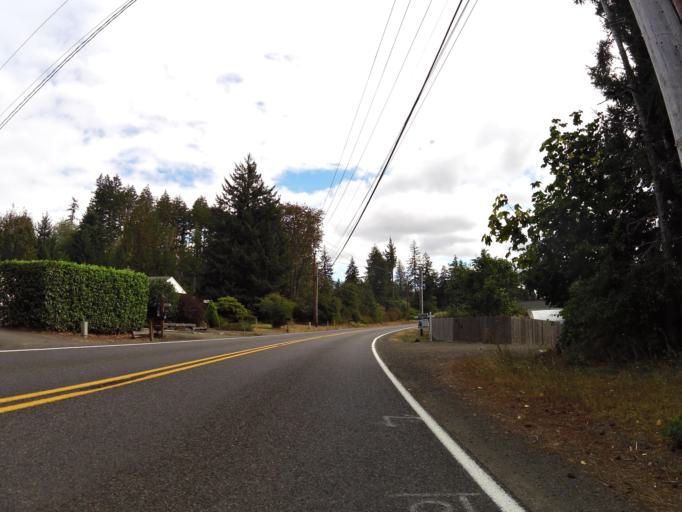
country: US
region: Washington
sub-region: Mason County
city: Shelton
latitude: 47.1808
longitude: -123.0923
